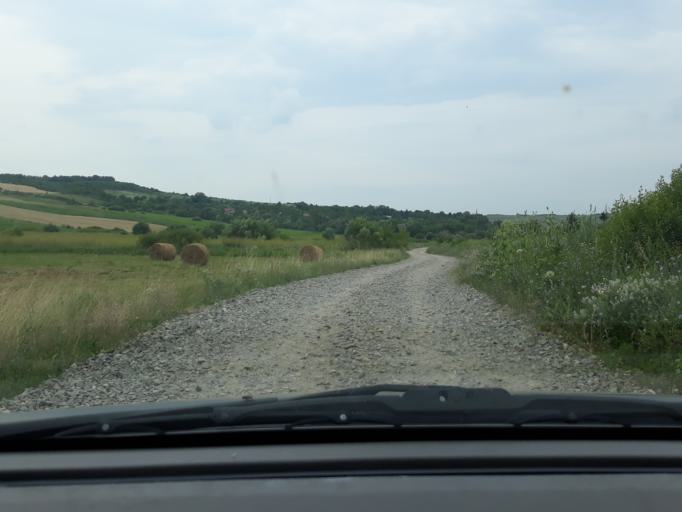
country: RO
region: Salaj
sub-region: Comuna Criseni
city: Criseni
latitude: 47.2664
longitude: 23.0669
